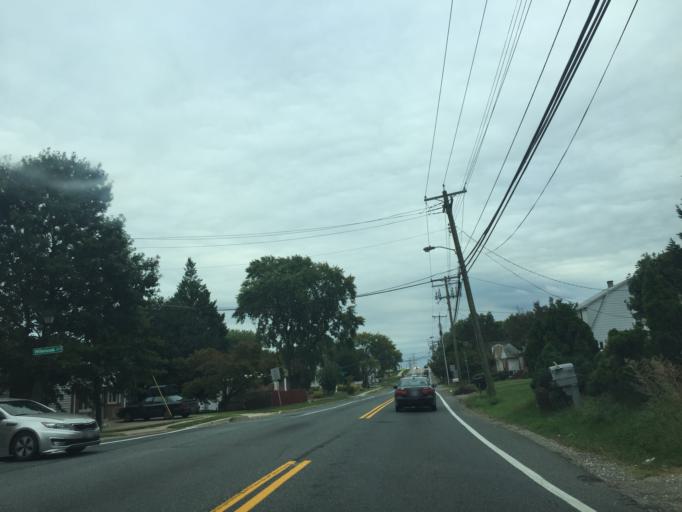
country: US
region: Maryland
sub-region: Baltimore County
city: Rossville
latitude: 39.3363
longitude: -76.5006
